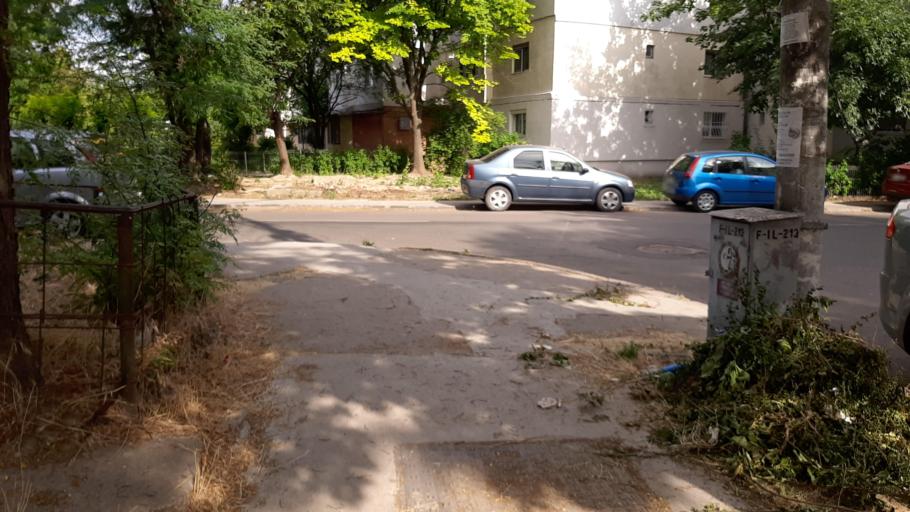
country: RO
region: Galati
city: Galati
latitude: 45.4430
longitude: 28.0270
